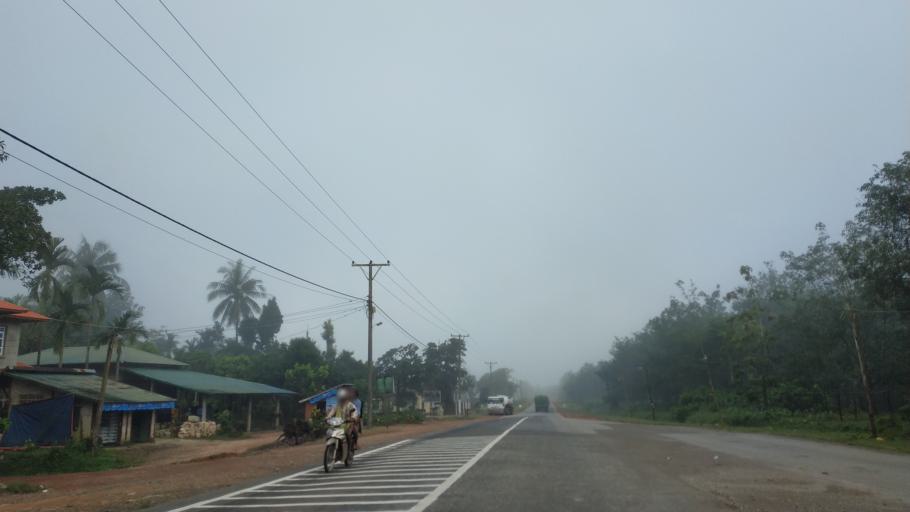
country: MM
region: Tanintharyi
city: Dawei
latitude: 14.1867
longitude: 98.2063
